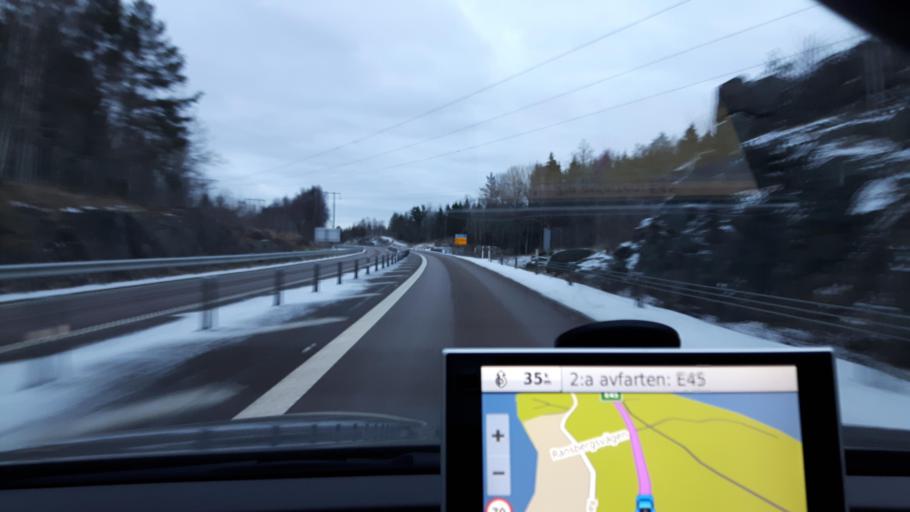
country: SE
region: Vaestra Goetaland
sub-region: Melleruds Kommun
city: Mellerud
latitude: 58.7817
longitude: 12.5101
